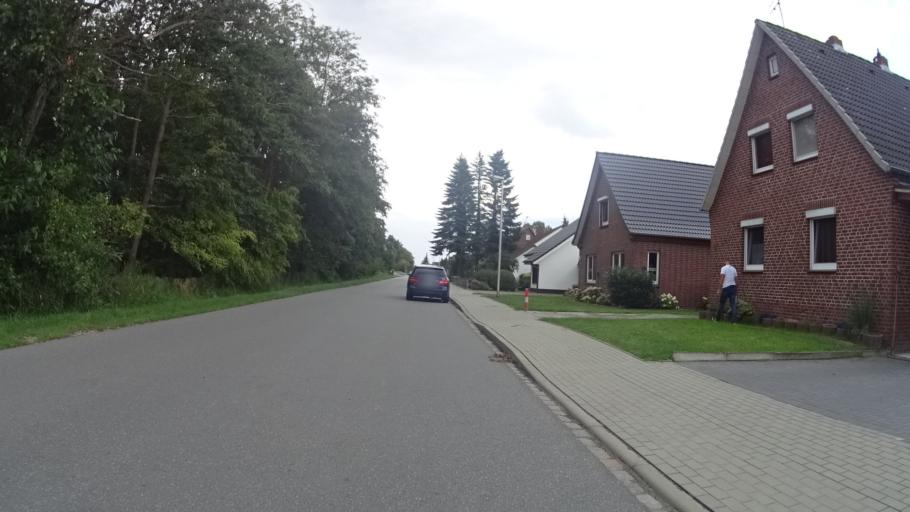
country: DE
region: Schleswig-Holstein
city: Gluckstadt
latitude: 53.7843
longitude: 9.4349
